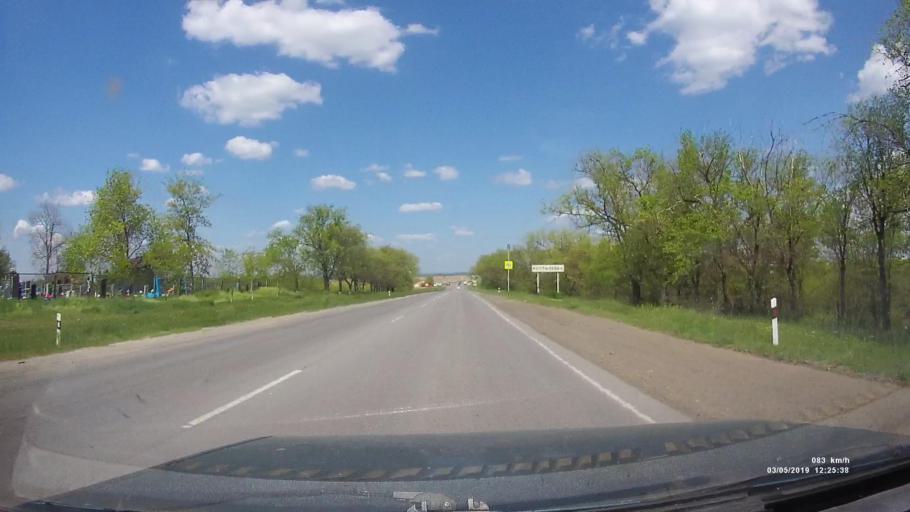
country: RU
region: Rostov
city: Semikarakorsk
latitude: 47.4355
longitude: 40.7117
